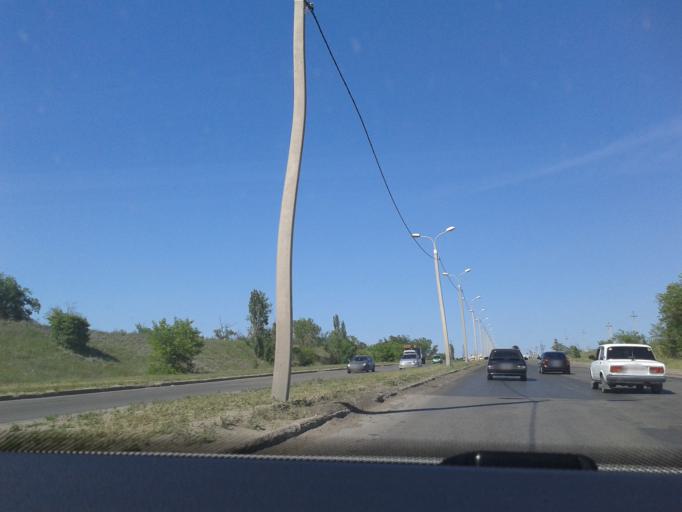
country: RU
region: Volgograd
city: Volgograd
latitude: 48.7382
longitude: 44.4597
